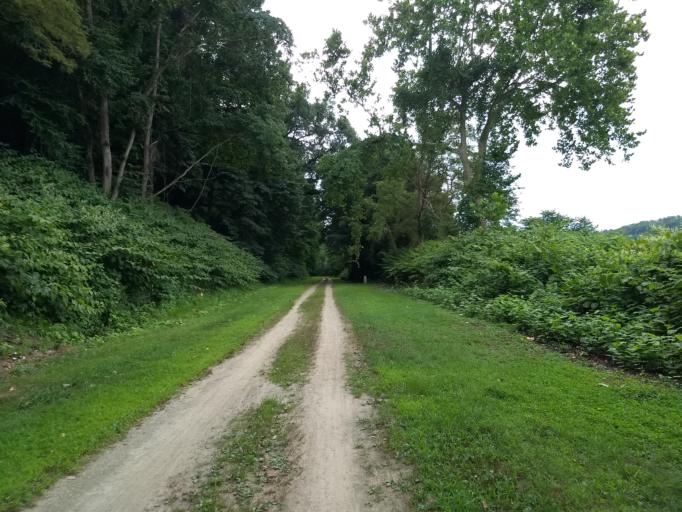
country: US
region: Pennsylvania
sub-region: Armstrong County
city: Freeport
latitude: 40.6329
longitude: -79.6939
